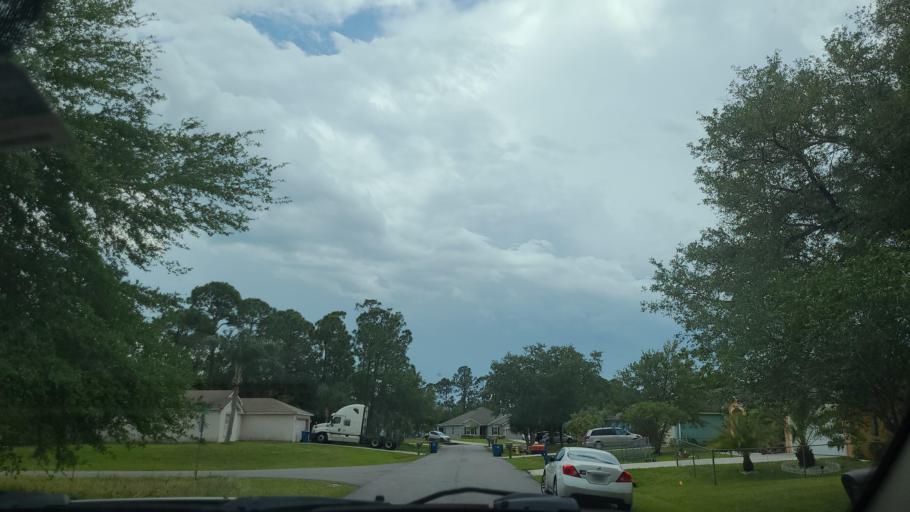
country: US
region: Florida
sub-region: Brevard County
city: Grant-Valkaria
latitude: 27.9360
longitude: -80.6266
